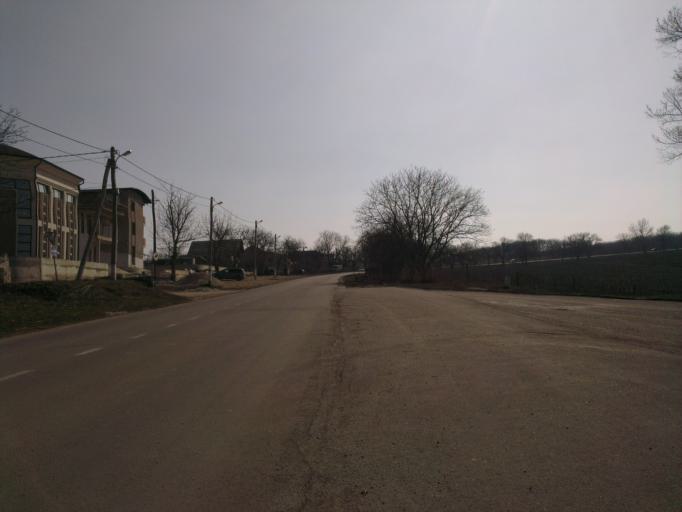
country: MD
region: Chisinau
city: Cricova
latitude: 47.1354
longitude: 28.8564
